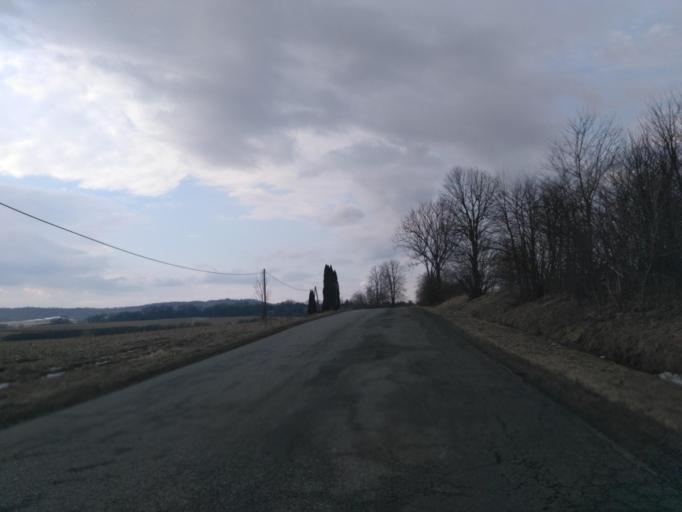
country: PL
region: Subcarpathian Voivodeship
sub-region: Powiat sanocki
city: Strachocina
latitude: 49.6099
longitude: 22.1121
